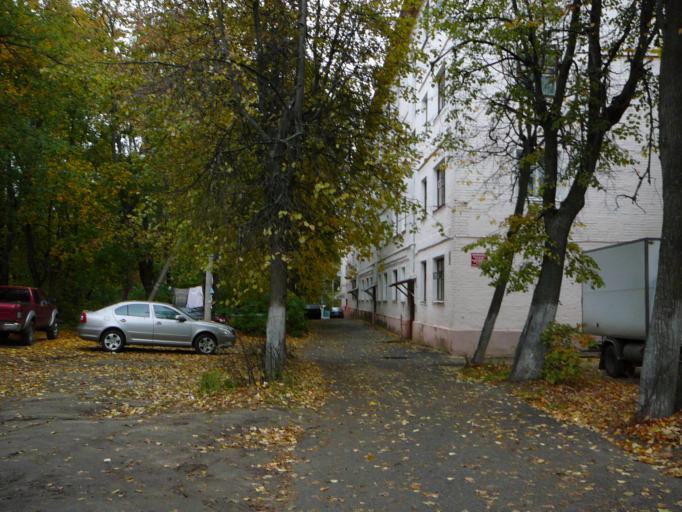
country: RU
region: Moskovskaya
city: Yegor'yevsk
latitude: 55.3887
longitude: 39.0300
